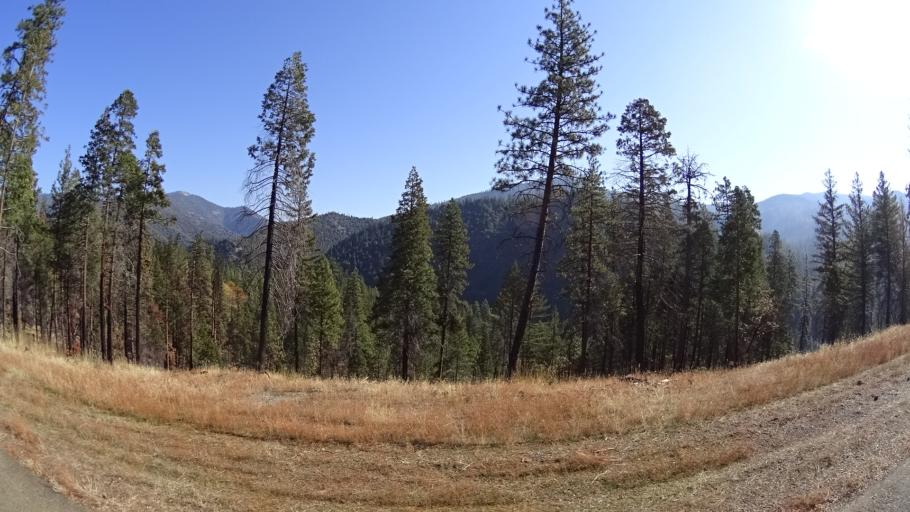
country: US
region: California
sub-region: Siskiyou County
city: Happy Camp
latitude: 41.7291
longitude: -123.0127
